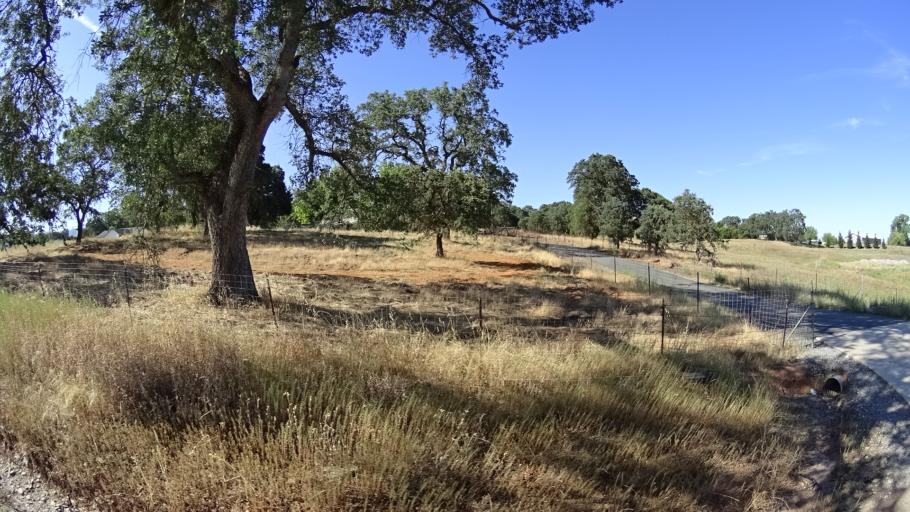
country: US
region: California
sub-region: Calaveras County
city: Valley Springs
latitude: 38.1841
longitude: -120.8180
